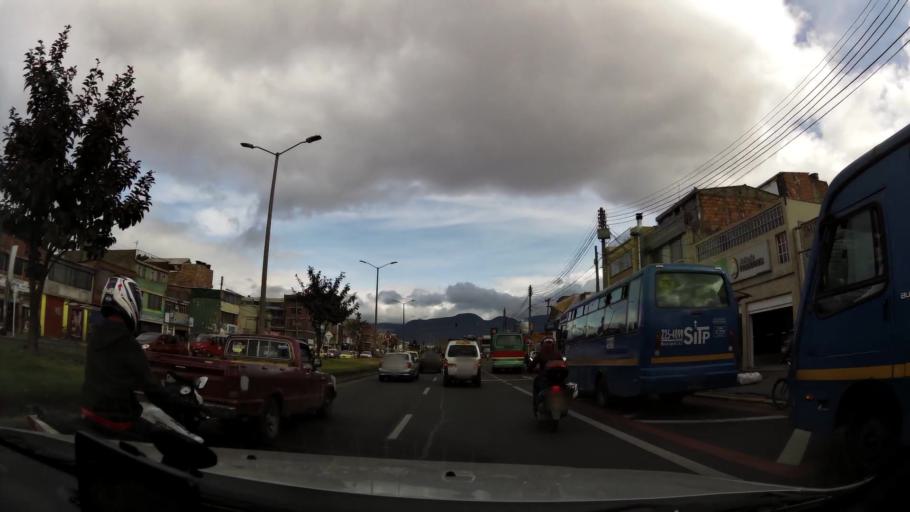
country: CO
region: Bogota D.C.
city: Bogota
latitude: 4.6070
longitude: -74.1268
